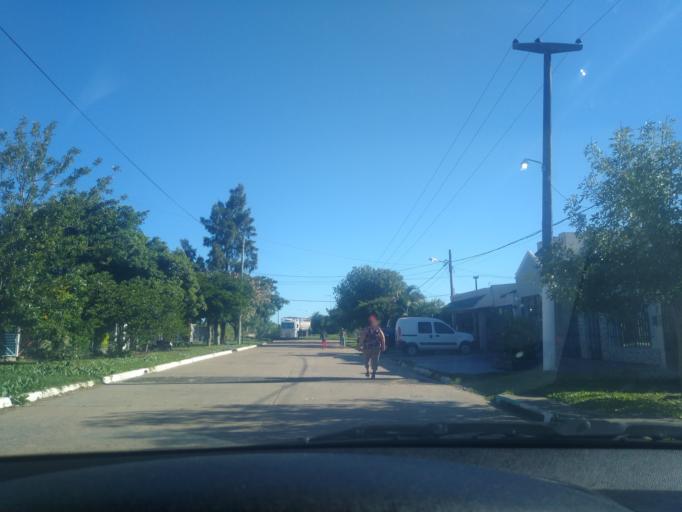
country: AR
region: Chaco
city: Puerto Vilelas
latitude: -27.5181
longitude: -58.9444
